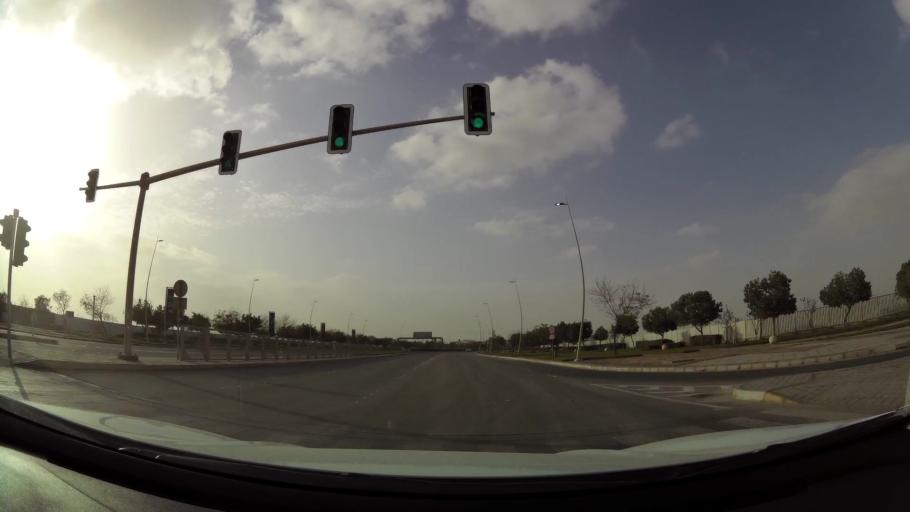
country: AE
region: Abu Dhabi
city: Abu Dhabi
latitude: 24.4903
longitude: 54.5933
